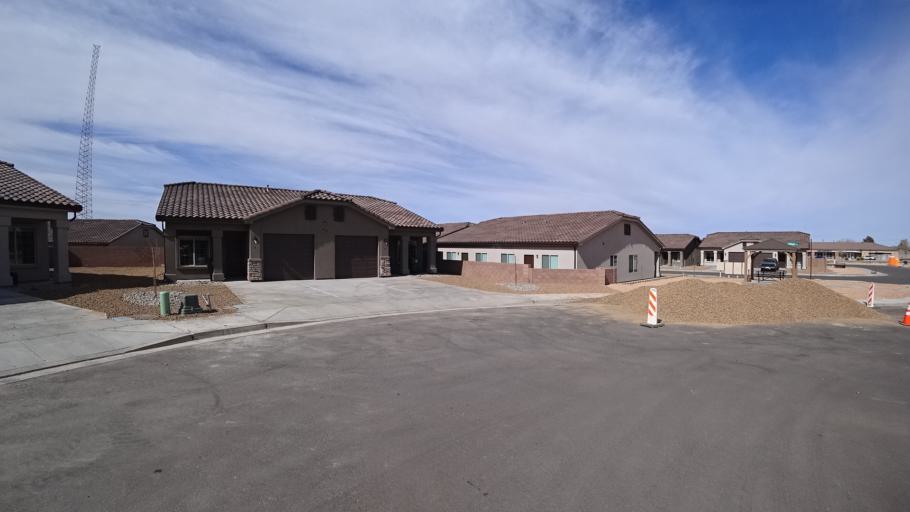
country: US
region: Arizona
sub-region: Mohave County
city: Kingman
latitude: 35.1900
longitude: -114.0186
